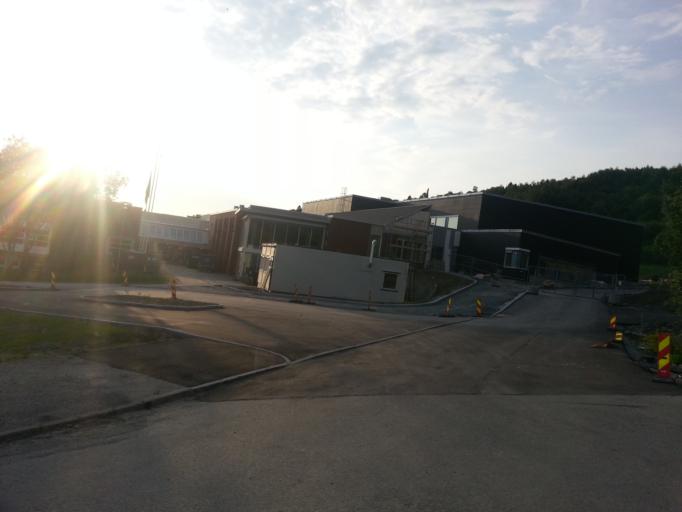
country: NO
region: Sor-Trondelag
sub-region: Malvik
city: Malvik
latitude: 63.4365
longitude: 10.6273
